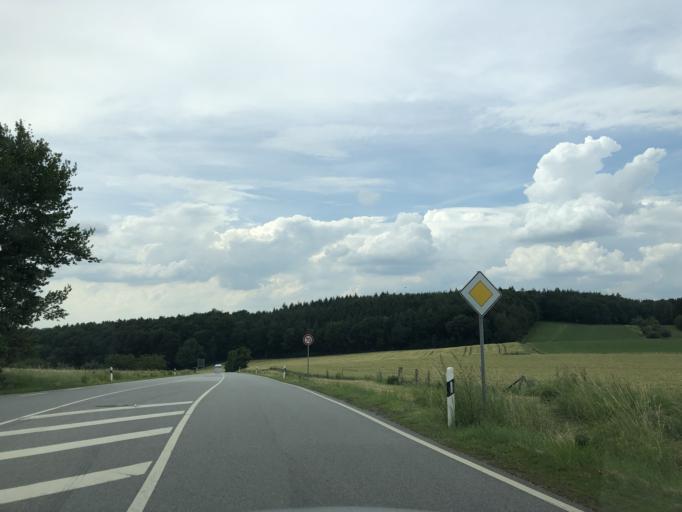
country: DE
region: Hesse
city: Lutzelbach
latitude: 49.7411
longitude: 8.7619
